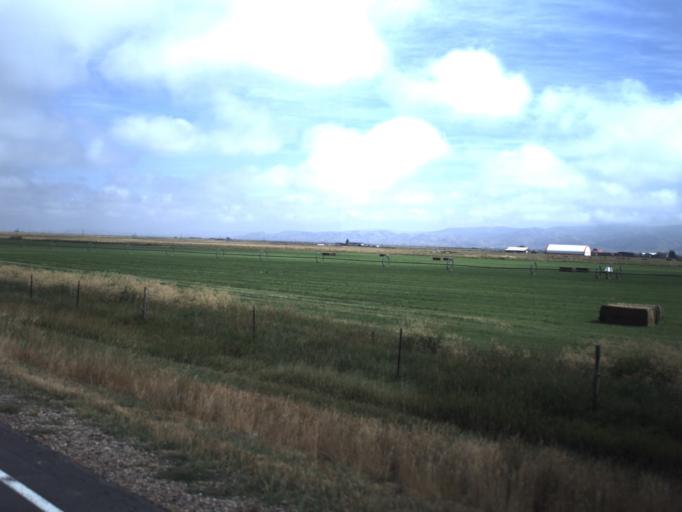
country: US
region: Utah
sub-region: Rich County
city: Randolph
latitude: 41.6818
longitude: -111.1803
